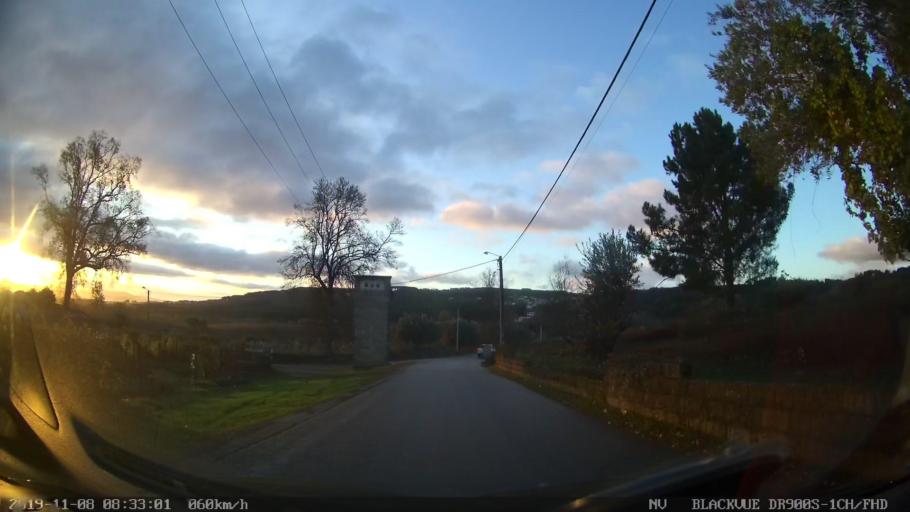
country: PT
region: Vila Real
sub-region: Sabrosa
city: Sabrosa
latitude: 41.2605
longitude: -7.5954
